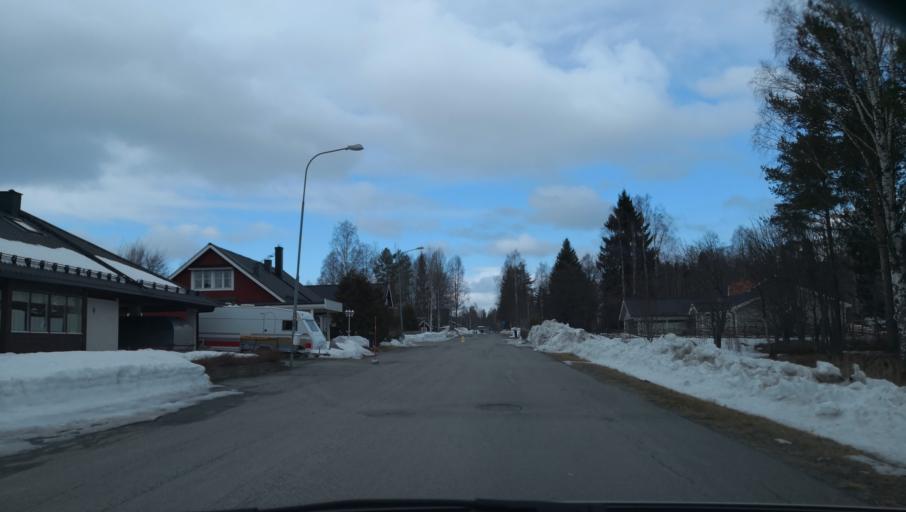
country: SE
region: Vaesterbotten
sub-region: Vannas Kommun
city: Vannasby
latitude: 63.9171
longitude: 19.8138
